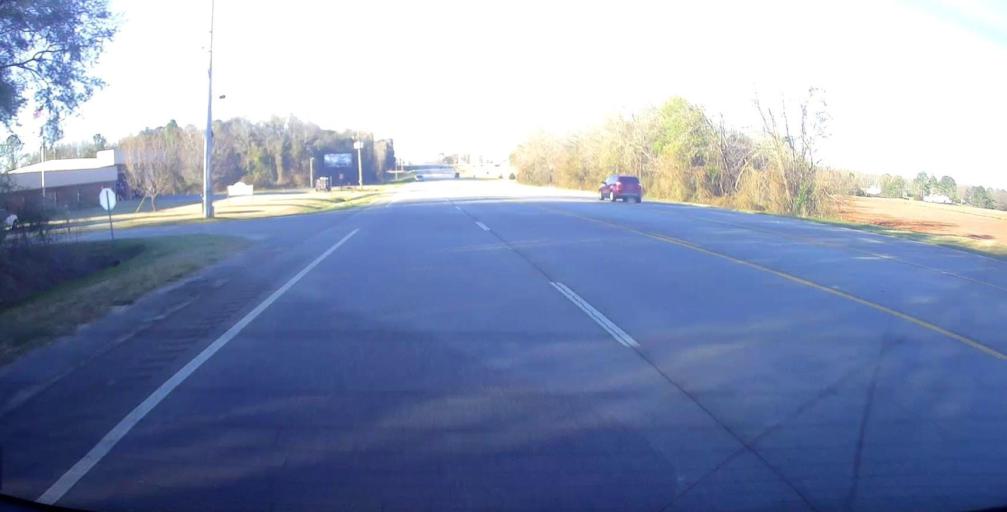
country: US
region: Georgia
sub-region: Lee County
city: Leesburg
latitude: 31.6742
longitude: -84.1729
